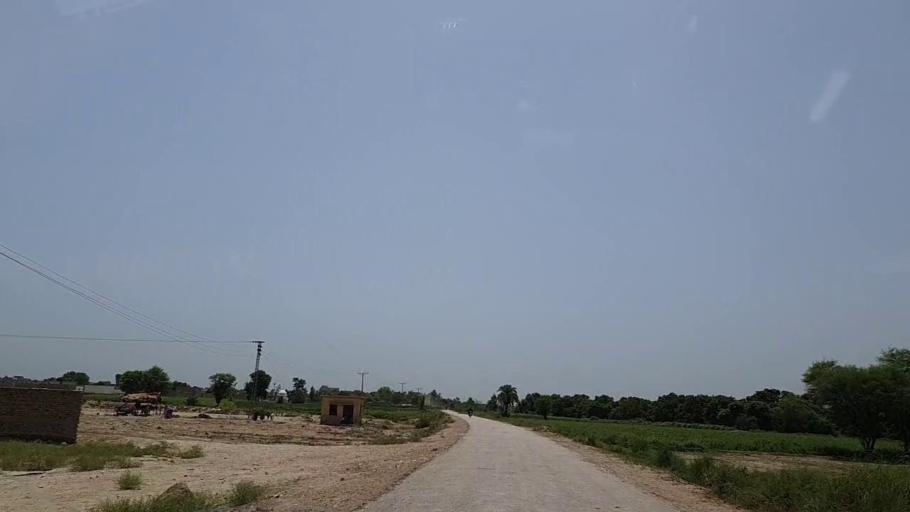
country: PK
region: Sindh
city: Tharu Shah
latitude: 26.9444
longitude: 68.1067
